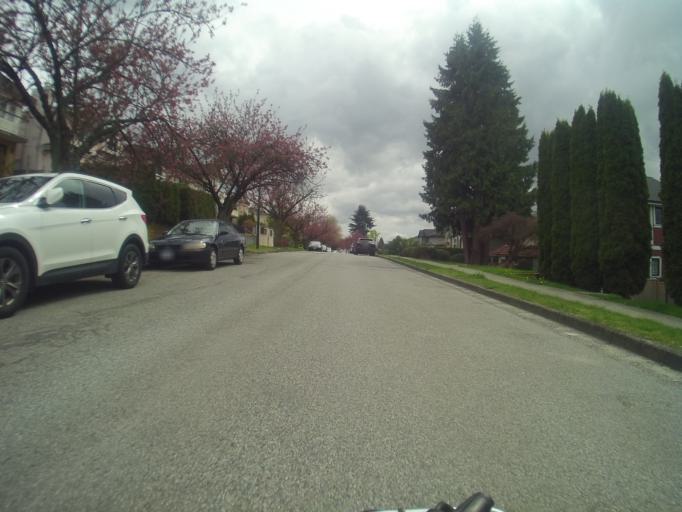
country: CA
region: British Columbia
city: Vancouver
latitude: 49.2319
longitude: -123.0743
